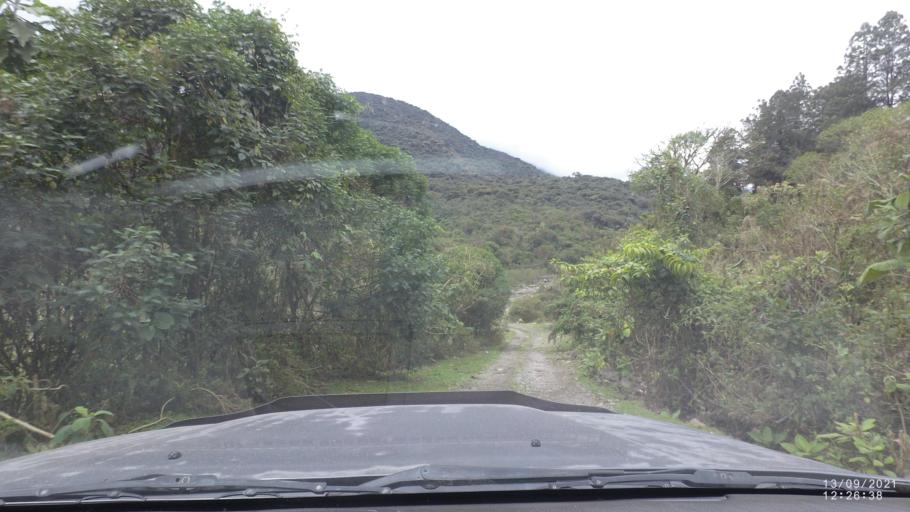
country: BO
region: Cochabamba
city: Colomi
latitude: -17.2536
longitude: -65.8157
